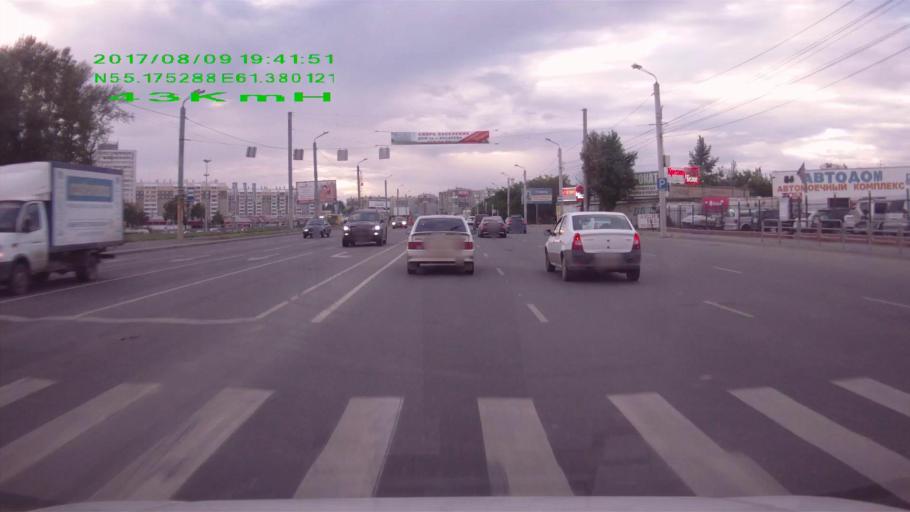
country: RU
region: Chelyabinsk
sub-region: Gorod Chelyabinsk
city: Chelyabinsk
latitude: 55.1755
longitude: 61.3794
